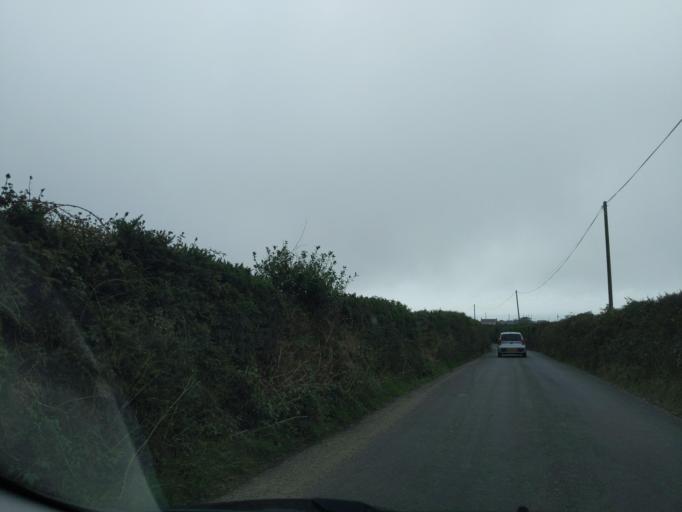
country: GB
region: England
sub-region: Cornwall
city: Germoe
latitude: 50.1023
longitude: -5.3581
